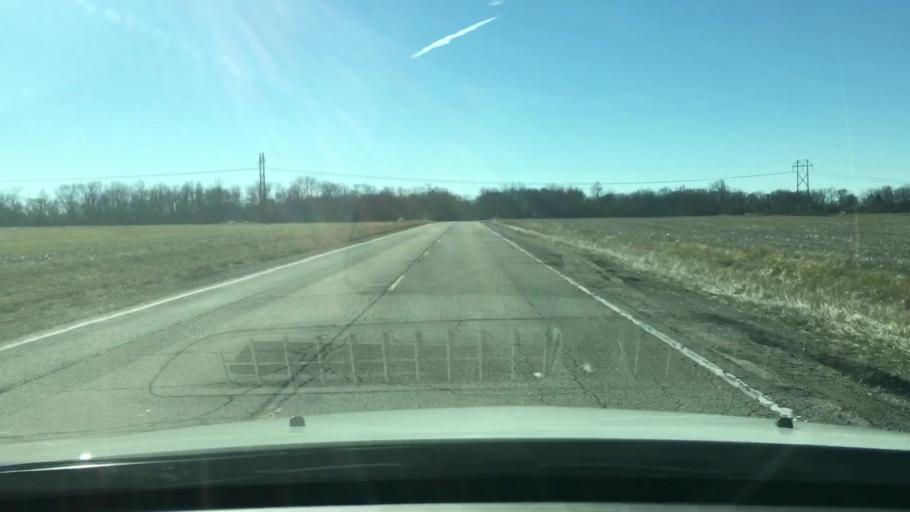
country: US
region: Illinois
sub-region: Mason County
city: Havana
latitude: 40.2922
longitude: -90.1545
